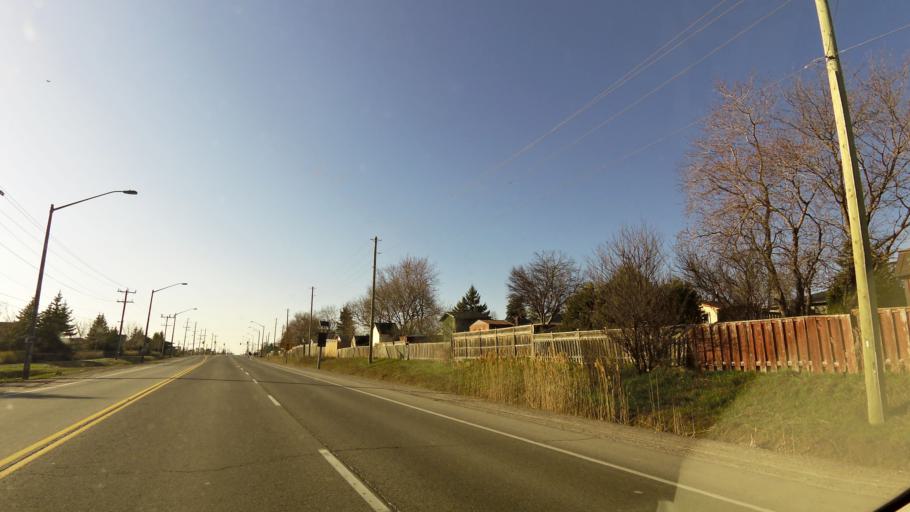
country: CA
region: Ontario
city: Brampton
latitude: 43.8858
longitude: -79.7467
